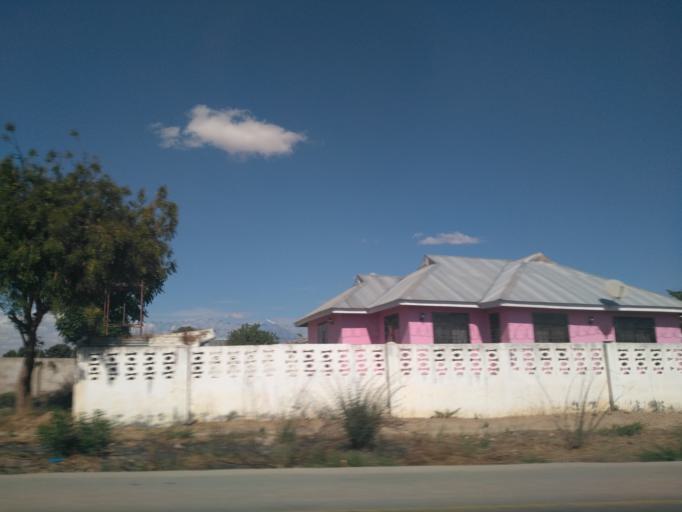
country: TZ
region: Dodoma
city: Dodoma
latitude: -6.1972
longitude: 35.7355
